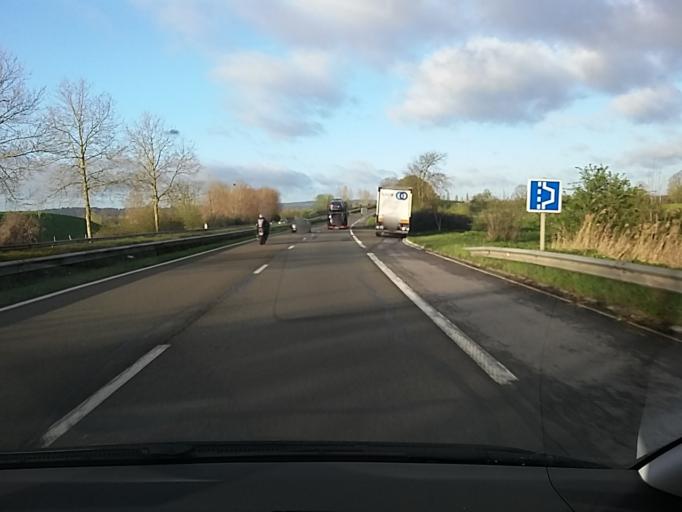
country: FR
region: Picardie
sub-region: Departement de l'Oise
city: Longueil-Sainte-Marie
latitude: 49.3393
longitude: 2.7341
